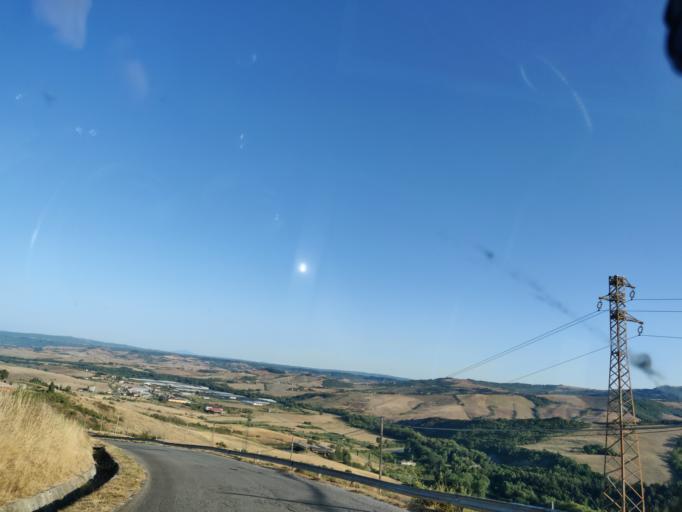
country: IT
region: Tuscany
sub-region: Provincia di Siena
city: Piancastagnaio
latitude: 42.8363
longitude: 11.7089
